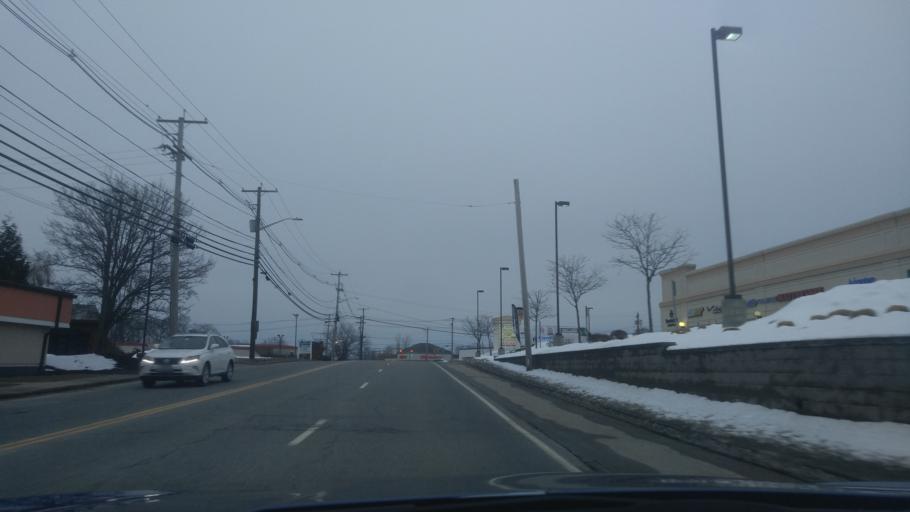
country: US
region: Rhode Island
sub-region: Providence County
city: Cranston
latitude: 41.7533
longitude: -71.4534
